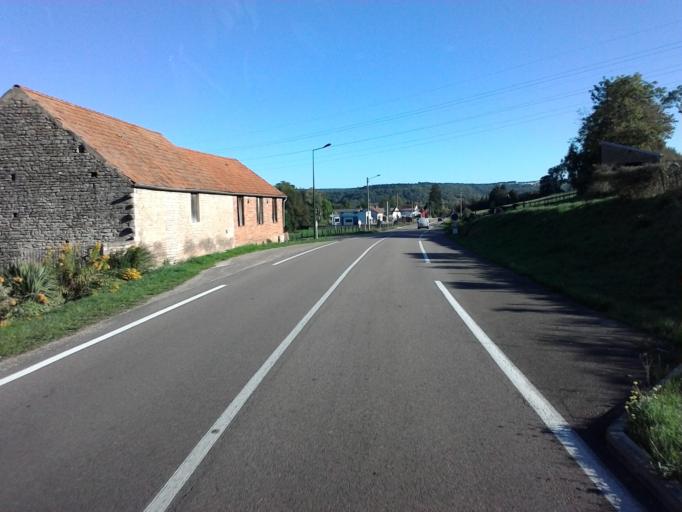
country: FR
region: Bourgogne
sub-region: Departement de la Cote-d'Or
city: Montbard
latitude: 47.6139
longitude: 4.3165
